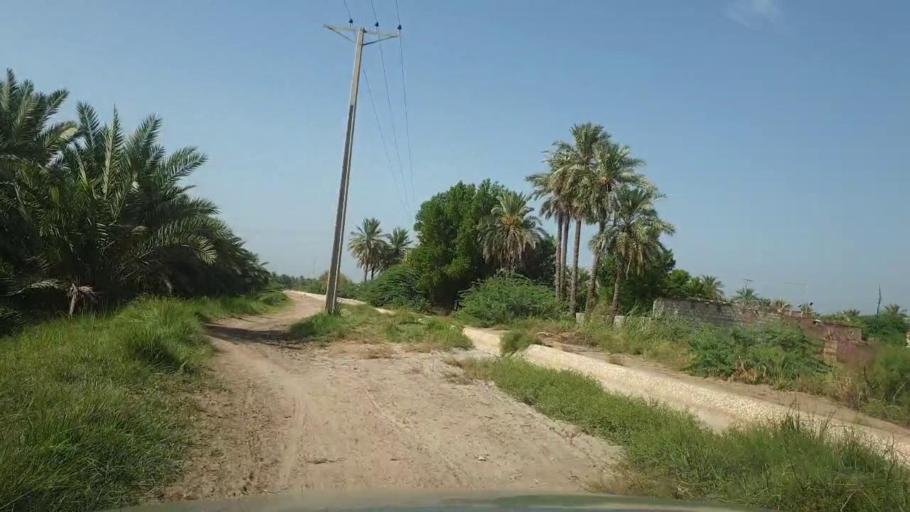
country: PK
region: Sindh
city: Rohri
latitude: 27.6545
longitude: 68.8794
